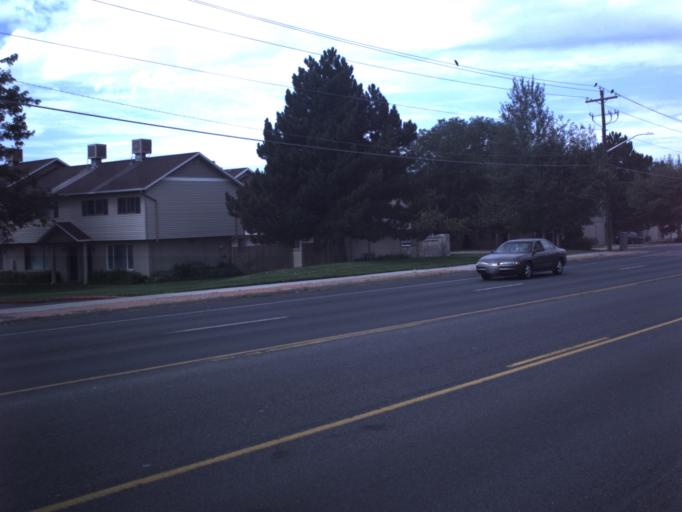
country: US
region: Utah
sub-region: Davis County
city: Clearfield
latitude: 41.0893
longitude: -112.0218
